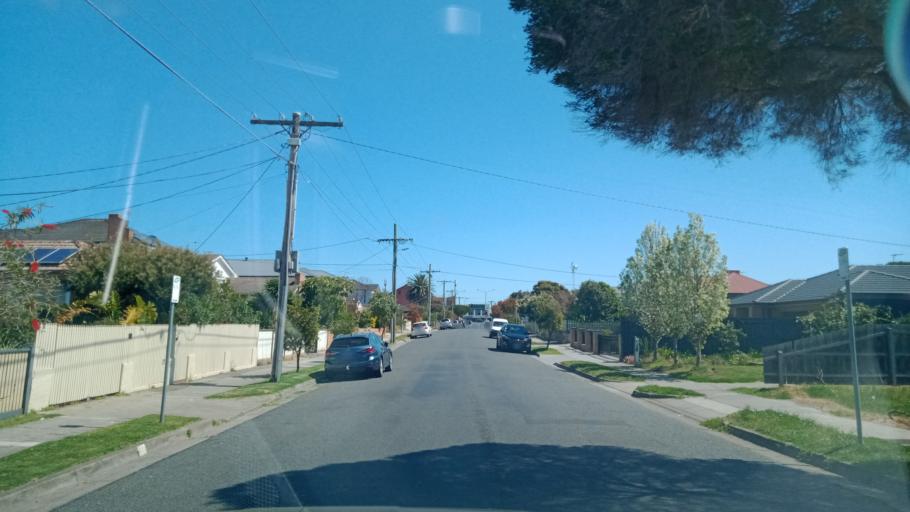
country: AU
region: Victoria
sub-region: Kingston
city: Chelsea
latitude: -38.0507
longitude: 145.1187
